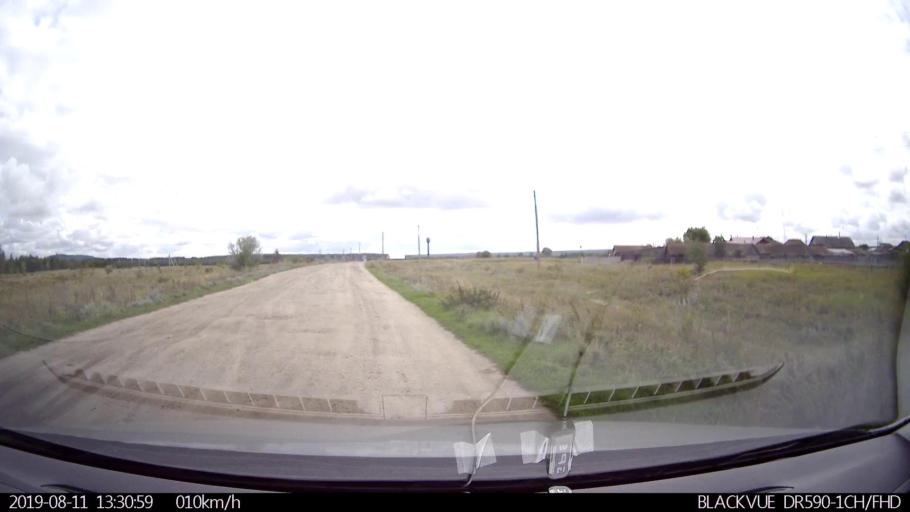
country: RU
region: Ulyanovsk
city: Ignatovka
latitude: 53.8601
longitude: 47.5998
